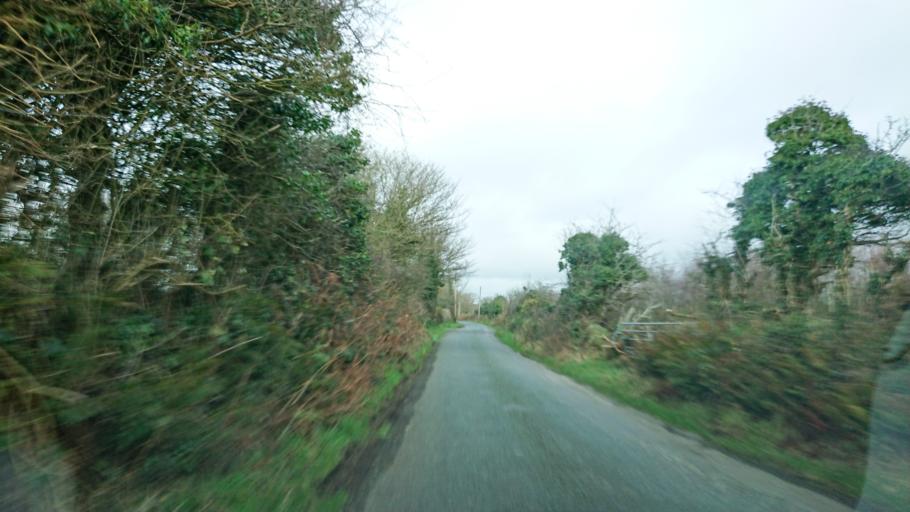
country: IE
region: Munster
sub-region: Waterford
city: Portlaw
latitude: 52.1611
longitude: -7.3065
